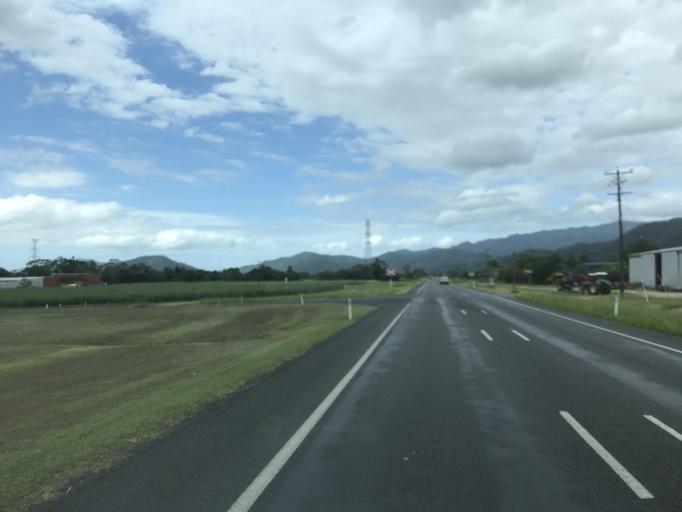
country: AU
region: Queensland
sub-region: Cassowary Coast
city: Innisfail
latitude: -17.7863
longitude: 146.0222
